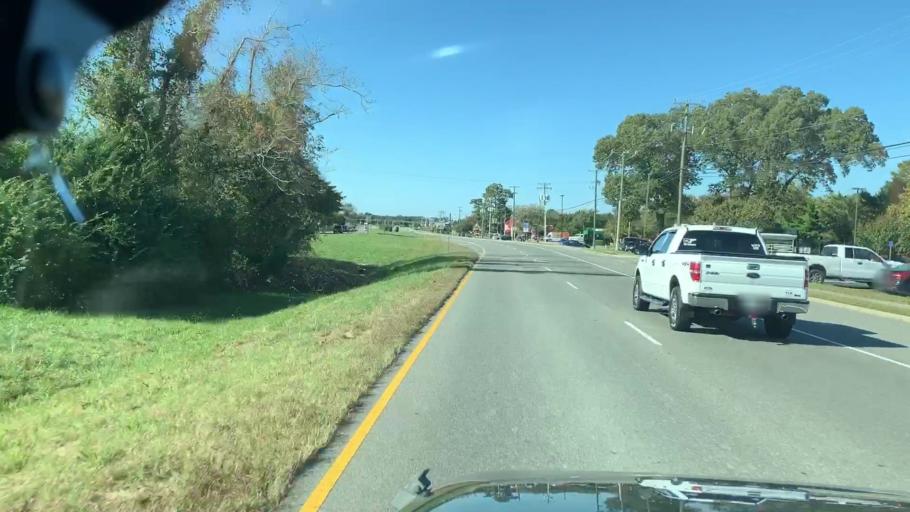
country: US
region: Virginia
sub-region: James City County
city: Williamsburg
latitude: 37.3440
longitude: -76.7570
